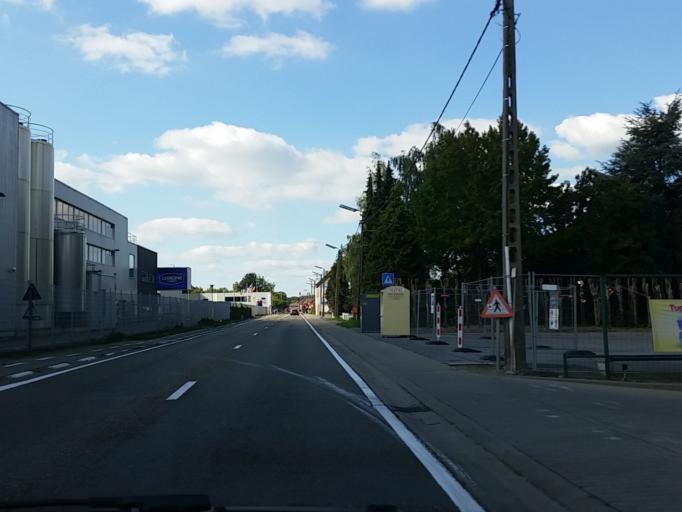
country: BE
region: Flanders
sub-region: Provincie Vlaams-Brabant
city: Rotselaar
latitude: 50.9426
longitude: 4.7308
